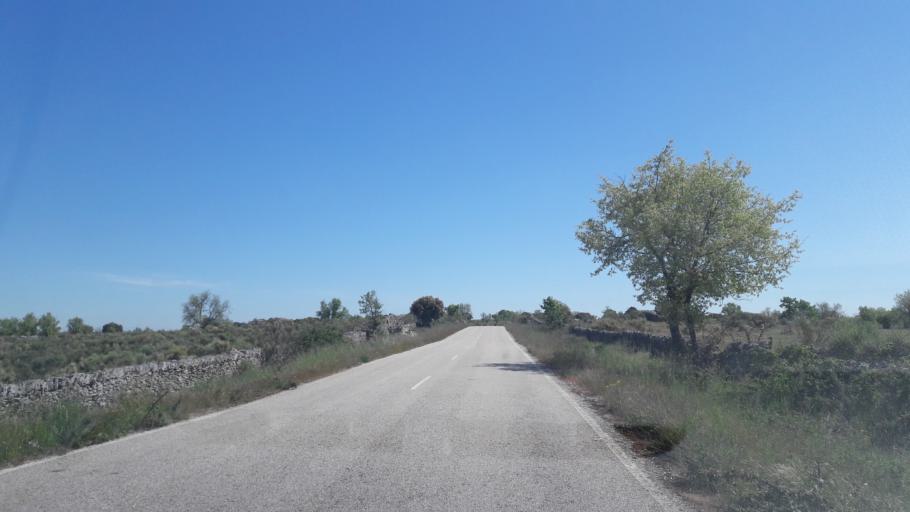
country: ES
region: Castille and Leon
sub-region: Provincia de Salamanca
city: Villarmuerto
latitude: 41.0463
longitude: -6.3864
